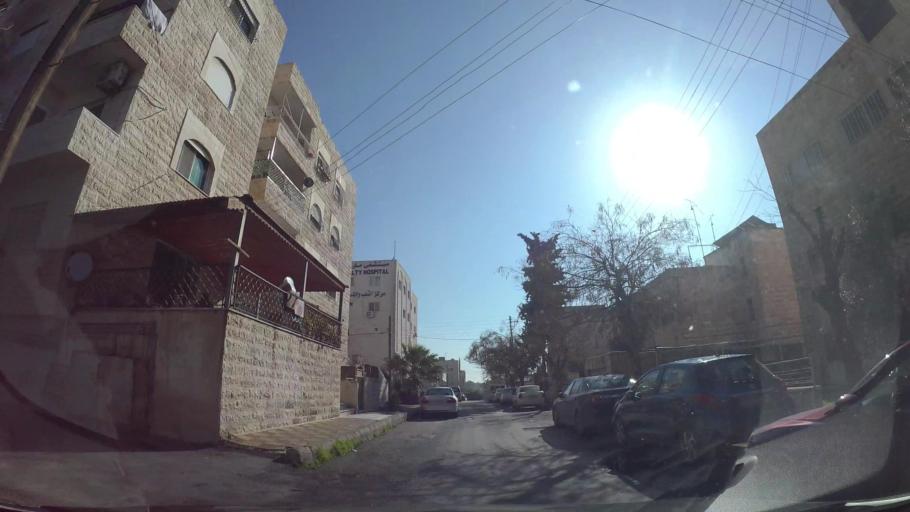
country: JO
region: Amman
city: Amman
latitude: 31.9842
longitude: 35.9897
